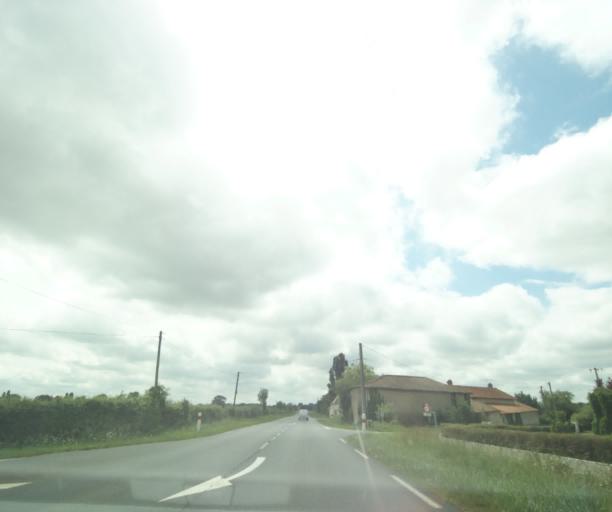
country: FR
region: Poitou-Charentes
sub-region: Departement des Deux-Sevres
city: Viennay
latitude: 46.7081
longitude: -0.2394
